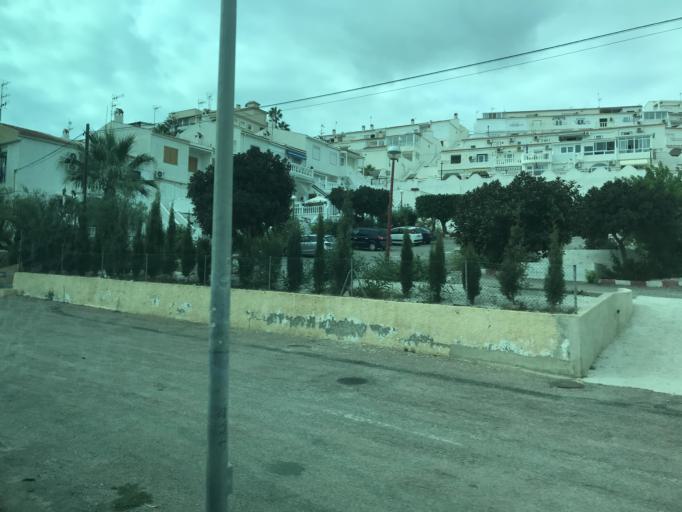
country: ES
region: Valencia
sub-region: Provincia de Alicante
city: Torrevieja
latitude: 38.0037
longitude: -0.6505
